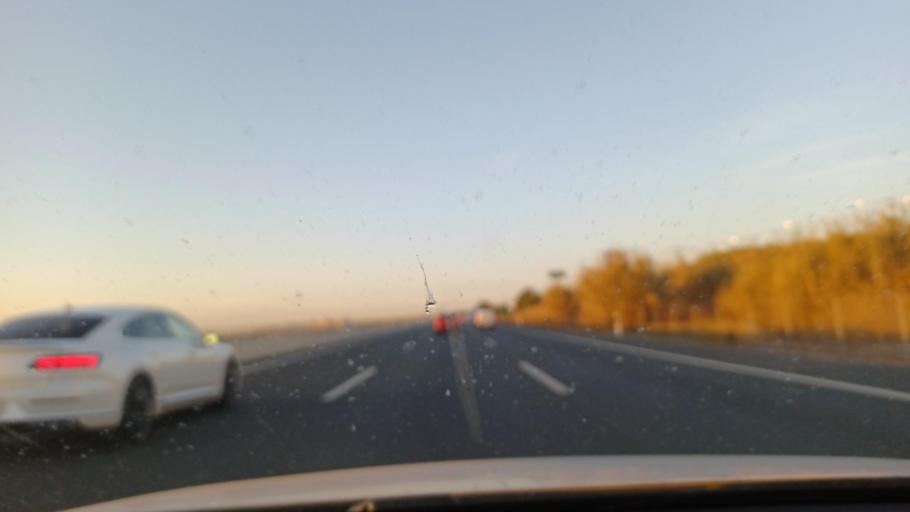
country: ES
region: Valencia
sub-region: Provincia de Valencia
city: Albuixech
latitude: 39.5396
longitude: -0.3050
